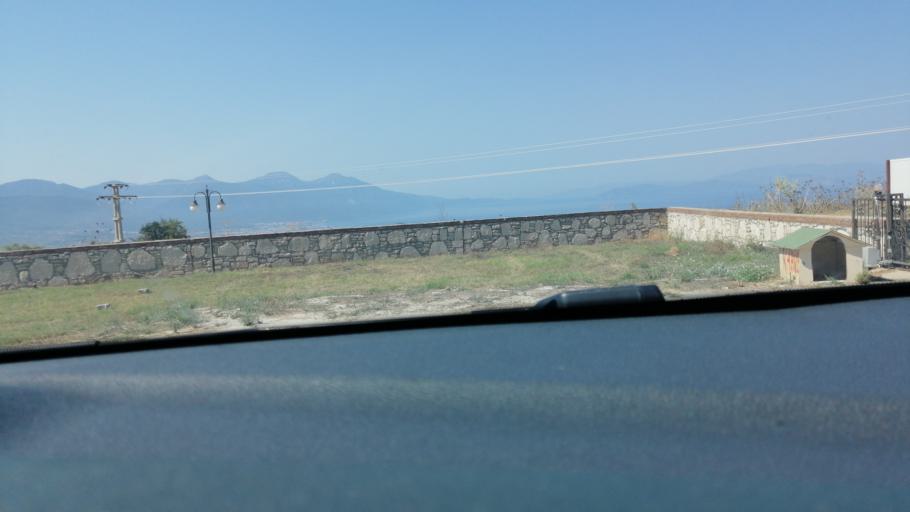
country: TR
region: Aydin
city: Davutlar
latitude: 37.7777
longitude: 27.3149
